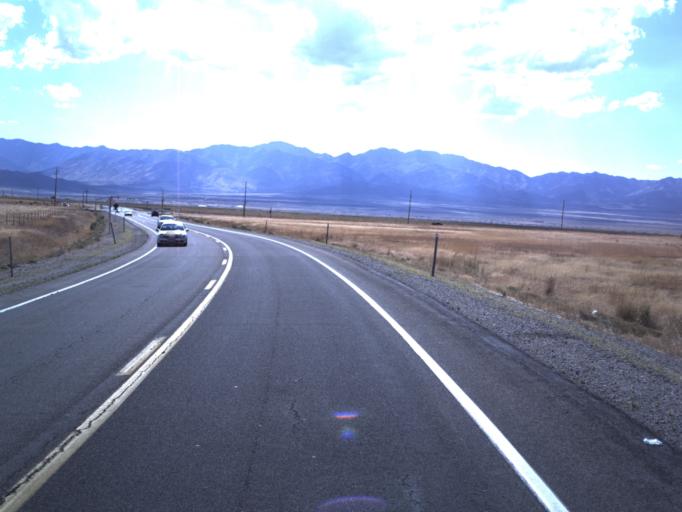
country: US
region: Utah
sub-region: Tooele County
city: Tooele
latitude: 40.5505
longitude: -112.3373
